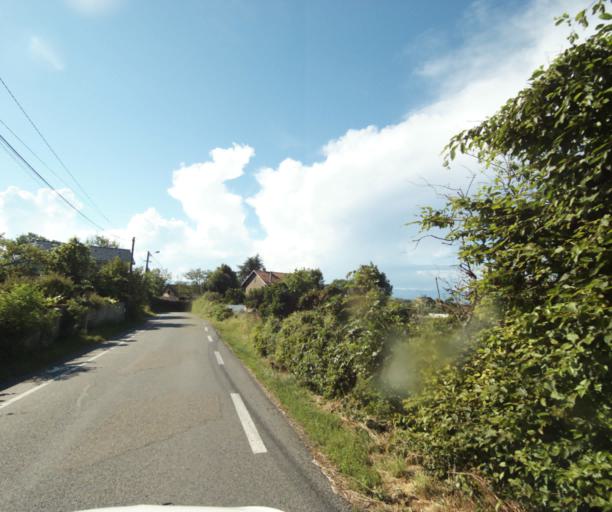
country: FR
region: Rhone-Alpes
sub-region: Departement de la Haute-Savoie
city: Sciez
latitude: 46.3276
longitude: 6.3581
